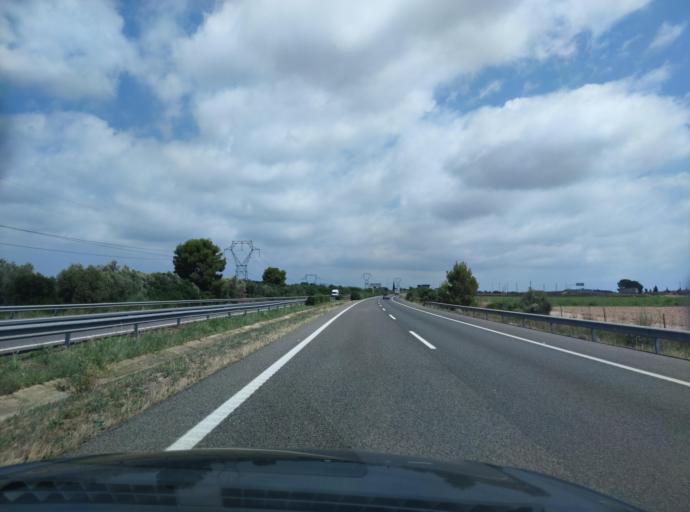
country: ES
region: Catalonia
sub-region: Provincia de Tarragona
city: Amposta
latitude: 40.7460
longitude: 0.5942
